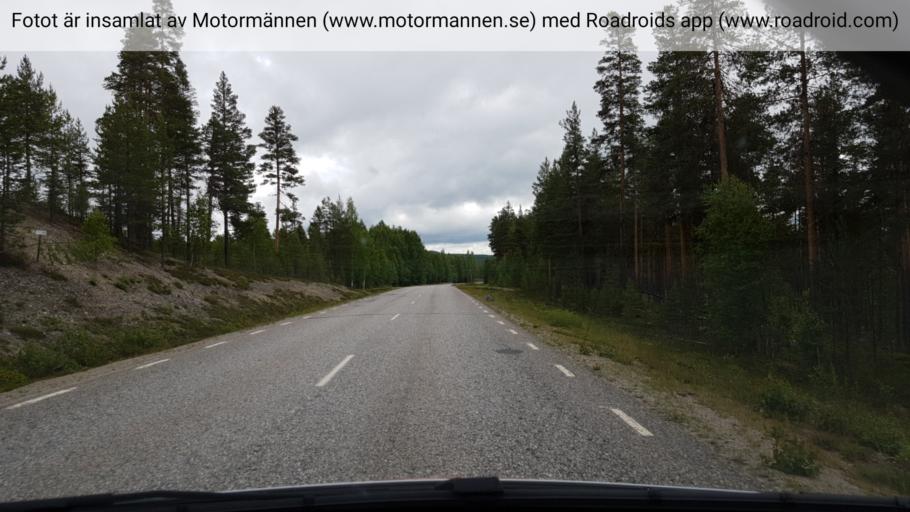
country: SE
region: Vaesterbotten
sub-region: Norsjo Kommun
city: Norsjoe
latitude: 64.6738
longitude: 19.2572
